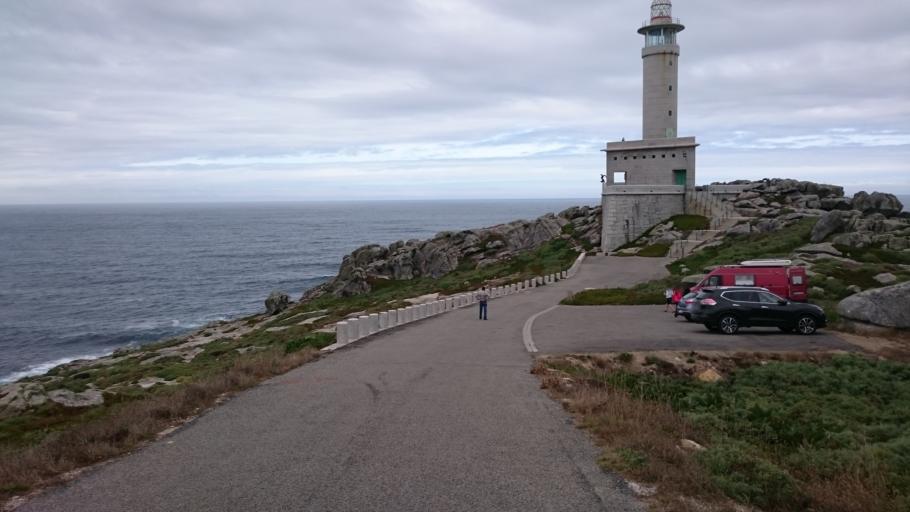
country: ES
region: Galicia
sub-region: Provincia da Coruna
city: Malpica
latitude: 43.3198
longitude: -8.9092
